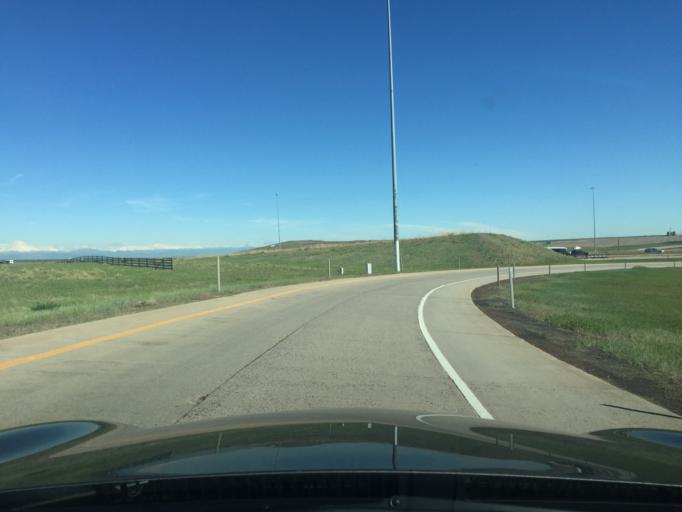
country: US
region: Colorado
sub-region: Adams County
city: Aurora
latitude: 39.8323
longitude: -104.7498
